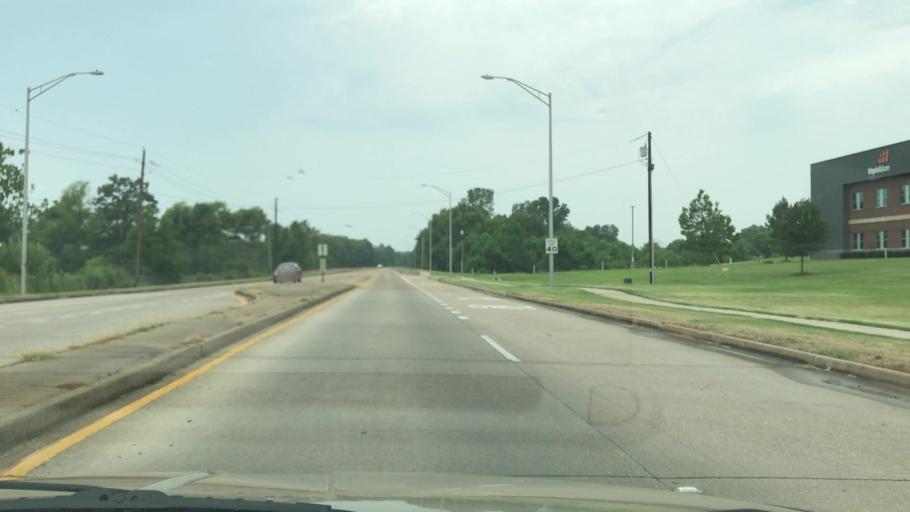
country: US
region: Louisiana
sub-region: Bossier Parish
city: Bossier City
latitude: 32.4758
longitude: -93.6942
